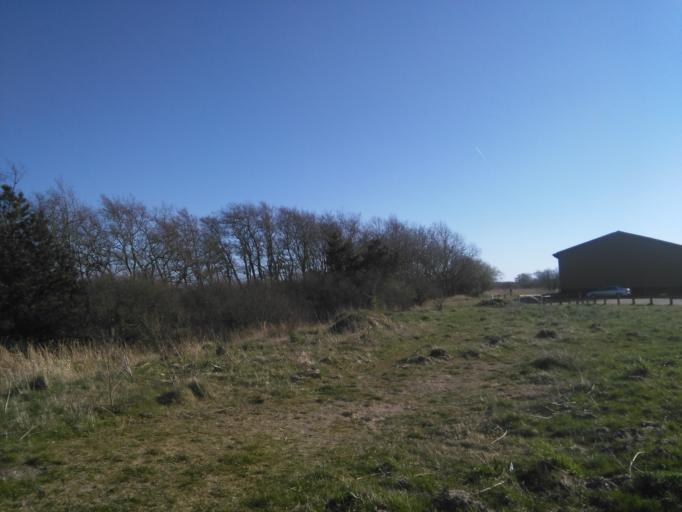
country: DK
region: South Denmark
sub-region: Varde Kommune
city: Oksbol
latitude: 55.7025
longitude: 8.2087
